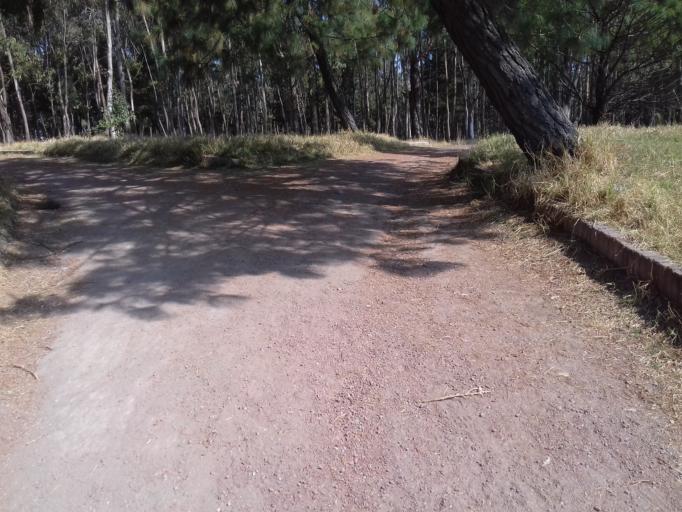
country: MX
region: Mexico
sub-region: Toluca
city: San Antonio Buenavista
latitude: 19.2764
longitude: -99.6975
